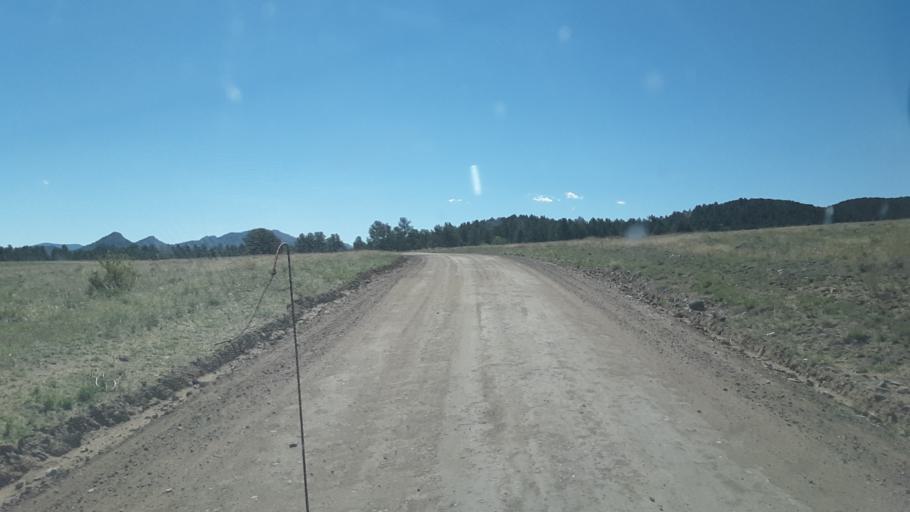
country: US
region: Colorado
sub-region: Custer County
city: Westcliffe
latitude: 38.2019
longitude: -105.4471
